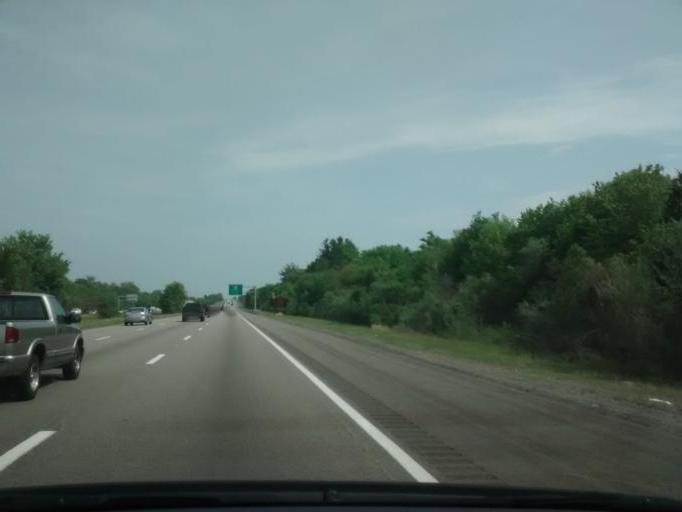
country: US
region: Massachusetts
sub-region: Bristol County
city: Mansfield Center
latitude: 42.0181
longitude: -71.2418
